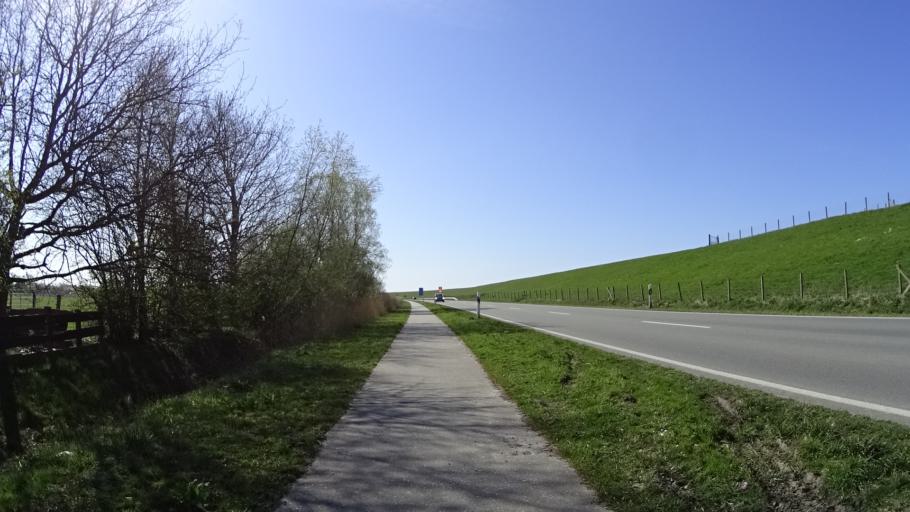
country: DE
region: Lower Saxony
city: Jemgum
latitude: 53.2410
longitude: 7.4073
